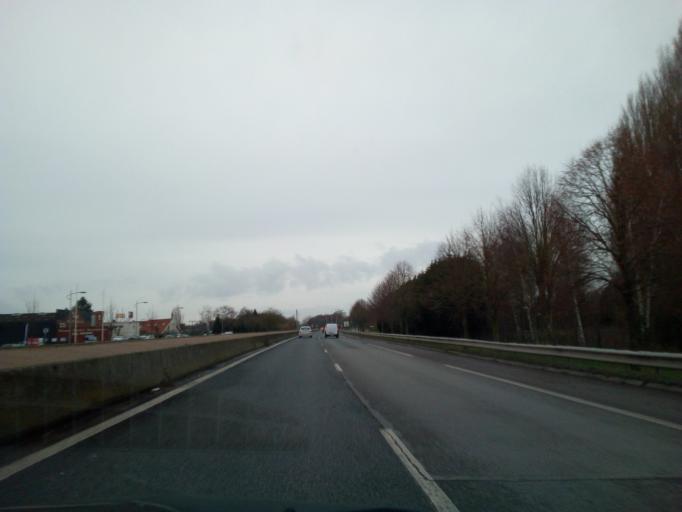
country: FR
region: Nord-Pas-de-Calais
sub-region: Departement du Pas-de-Calais
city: Beuvry
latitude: 50.5136
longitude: 2.6890
